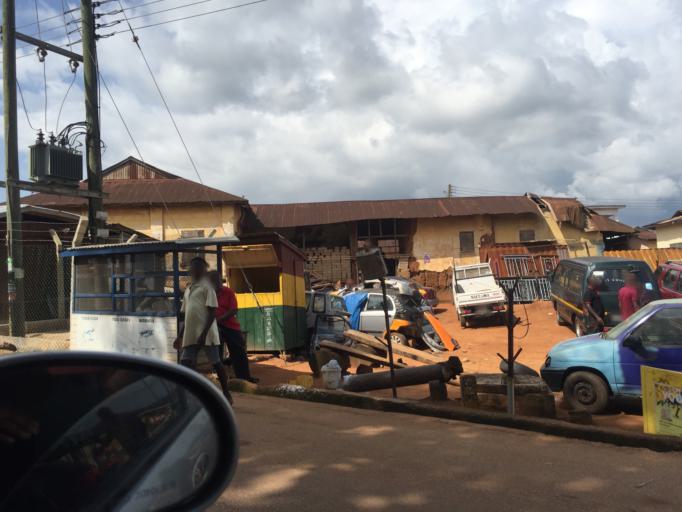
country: GH
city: Mpraeso
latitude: 6.5934
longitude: -0.7358
